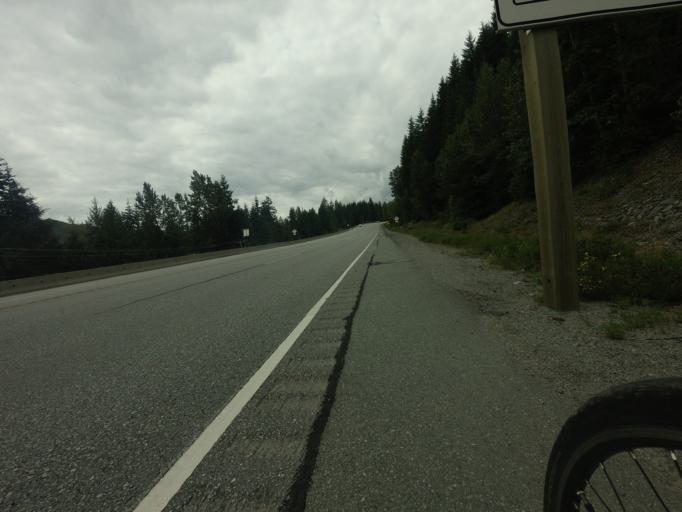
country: CA
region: British Columbia
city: Whistler
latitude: 50.0841
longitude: -123.0527
